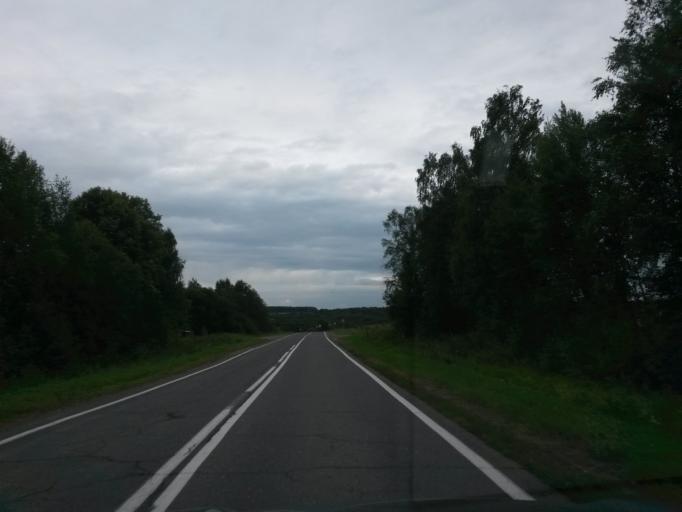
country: RU
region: Jaroslavl
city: Tutayev
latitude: 57.9446
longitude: 39.4962
